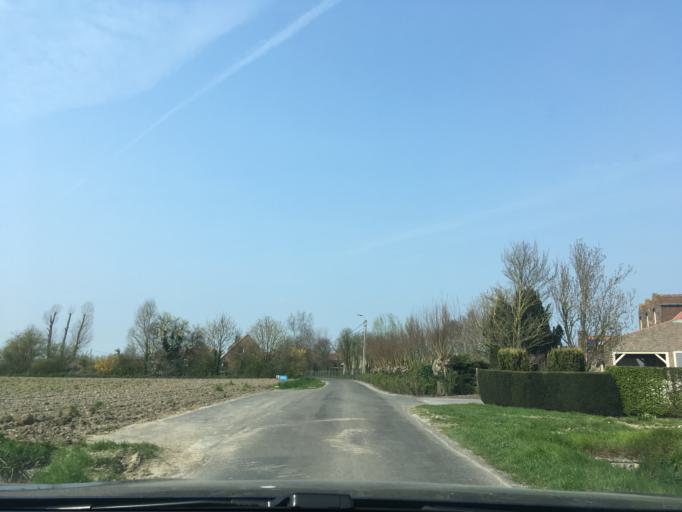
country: BE
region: Flanders
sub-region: Provincie West-Vlaanderen
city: Ardooie
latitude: 50.9860
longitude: 3.1922
